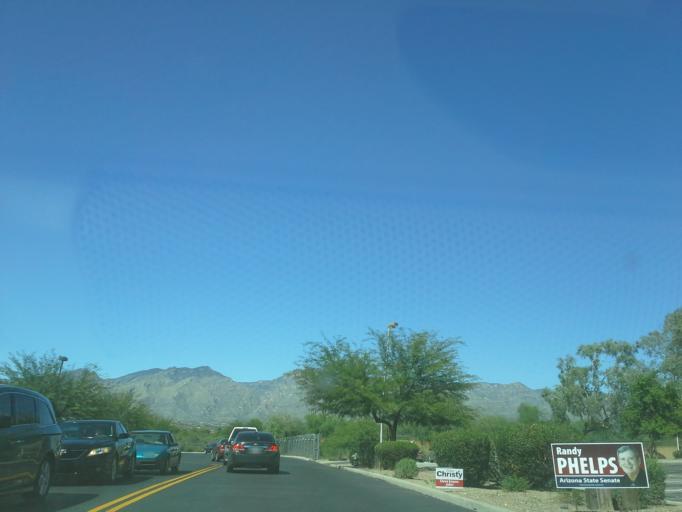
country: US
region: Arizona
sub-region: Pima County
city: Tucson
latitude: 32.2509
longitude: -110.8579
